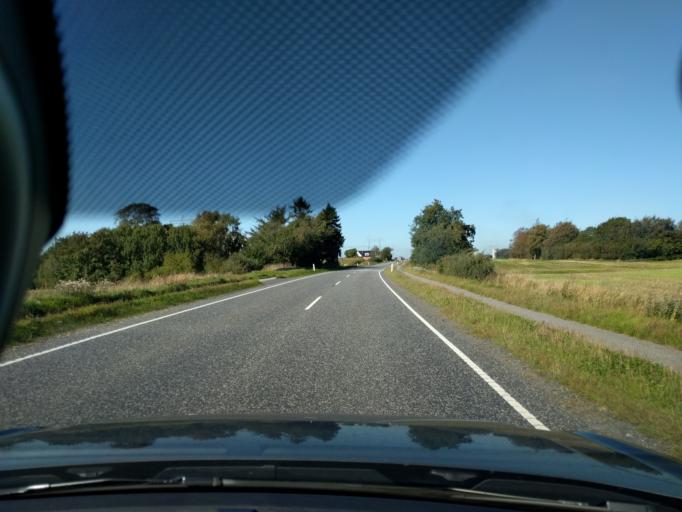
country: DK
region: North Denmark
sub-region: Vesthimmerland Kommune
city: Alestrup
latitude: 56.7170
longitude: 9.6128
